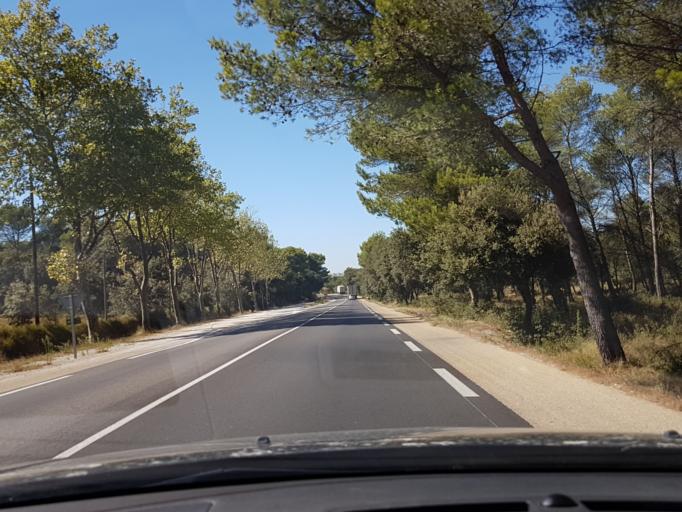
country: FR
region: Provence-Alpes-Cote d'Azur
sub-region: Departement du Vaucluse
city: Cavaillon
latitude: 43.8118
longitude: 5.0221
